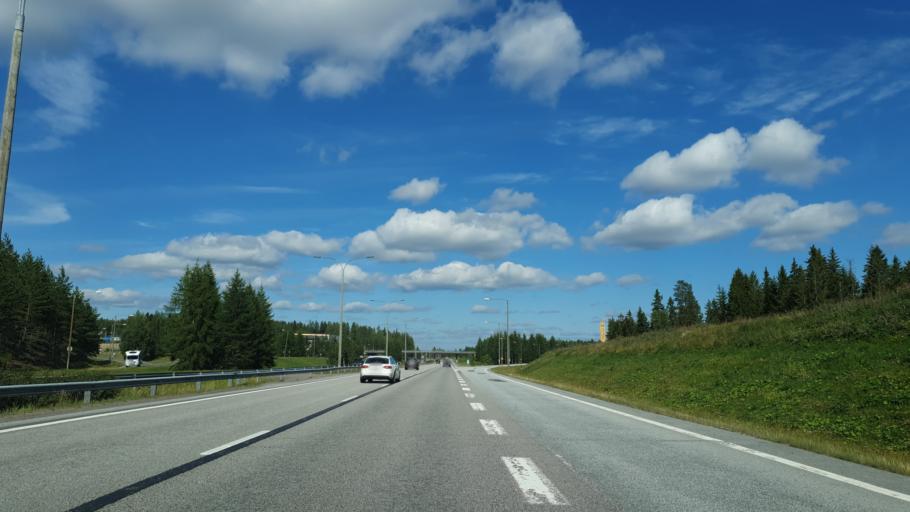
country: FI
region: Central Finland
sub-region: Jyvaeskylae
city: Muurame
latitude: 62.1867
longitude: 25.6927
